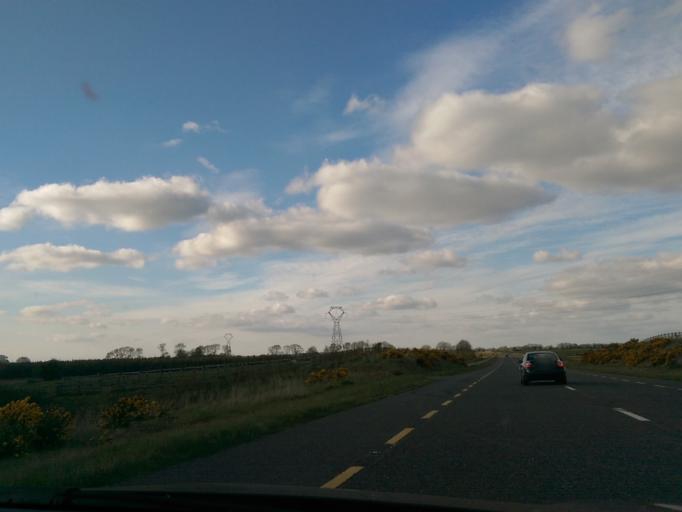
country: IE
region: Connaught
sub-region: County Galway
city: Loughrea
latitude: 53.2388
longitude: -8.5942
